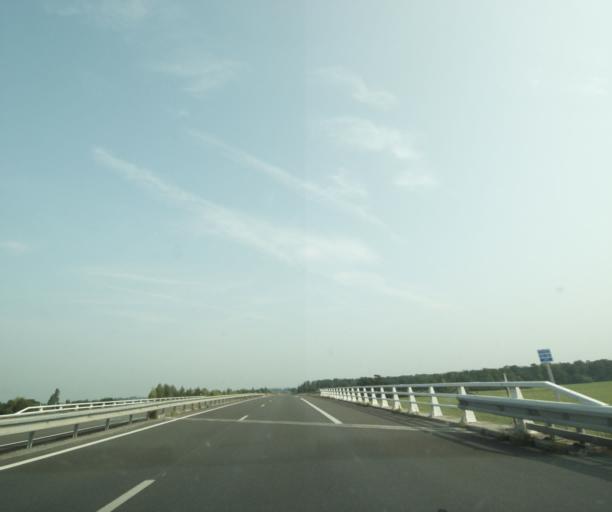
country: FR
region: Pays de la Loire
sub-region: Departement de la Sarthe
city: Beaumont-sur-Sarthe
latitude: 48.2032
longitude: 0.1749
